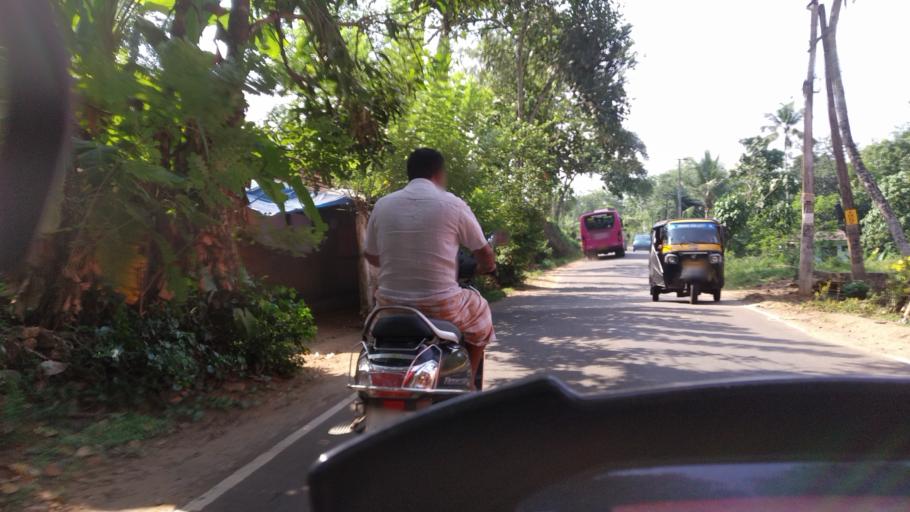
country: IN
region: Kerala
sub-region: Ernakulam
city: Piravam
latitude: 9.8123
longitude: 76.5619
